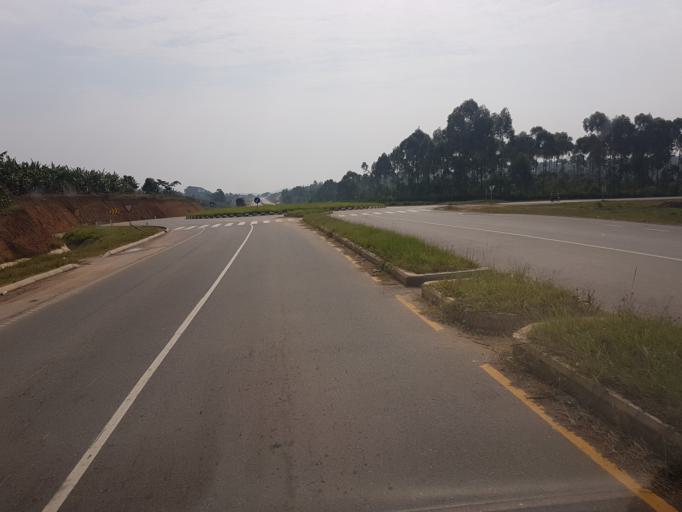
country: UG
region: Western Region
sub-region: Mbarara District
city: Bwizibwera
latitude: -0.6331
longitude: 30.5985
